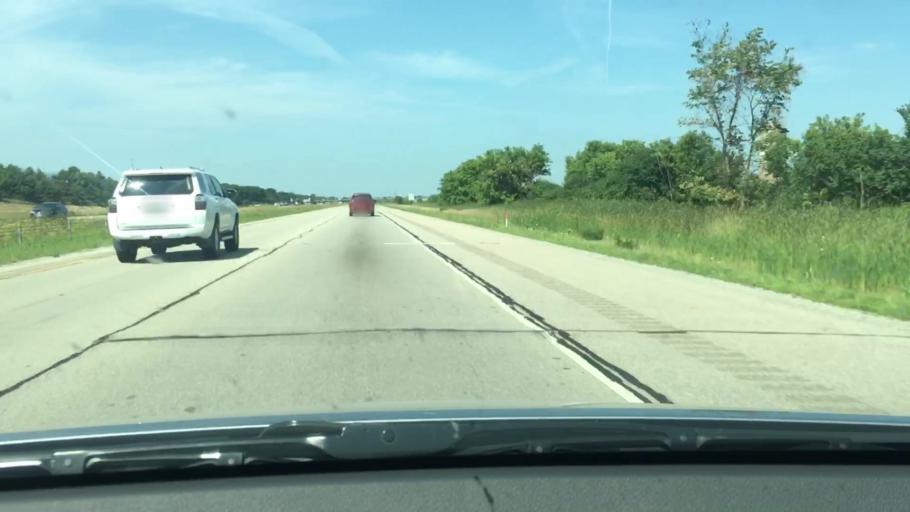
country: US
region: Wisconsin
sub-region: Outagamie County
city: Little Chute
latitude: 44.2981
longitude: -88.3364
